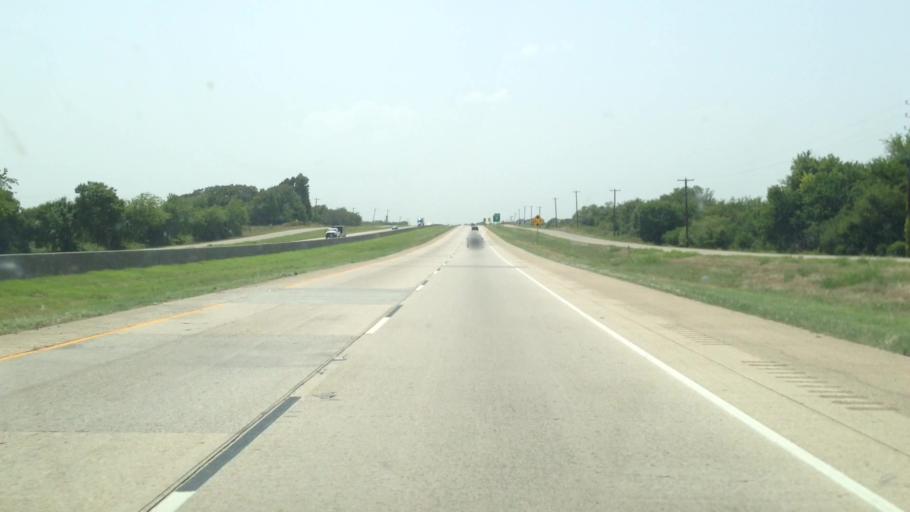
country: US
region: Texas
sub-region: Hopkins County
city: Sulphur Springs
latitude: 33.1212
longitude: -95.6595
